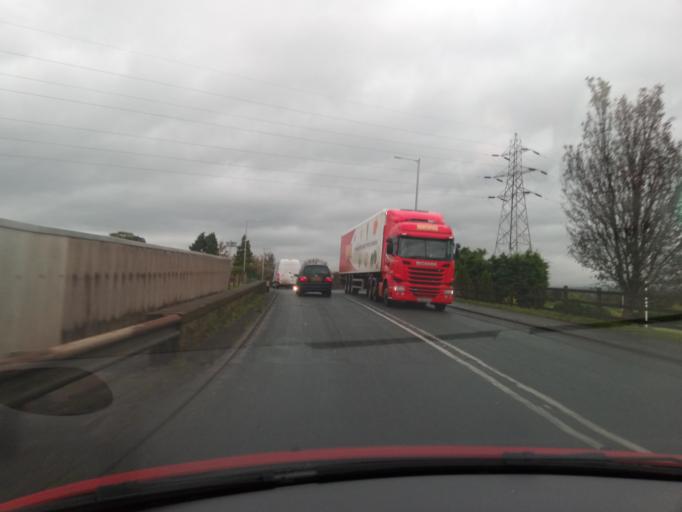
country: GB
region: England
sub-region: Lancashire
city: Catterall
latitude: 53.8364
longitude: -2.7391
